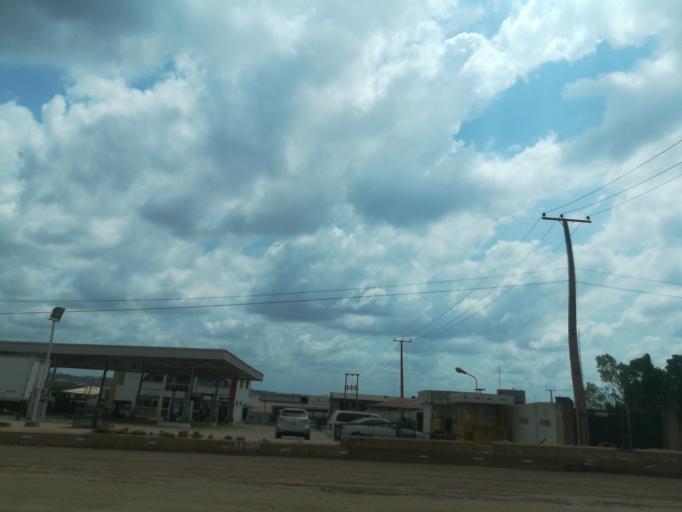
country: NG
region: Oyo
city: Ibadan
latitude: 7.4024
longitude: 3.9252
